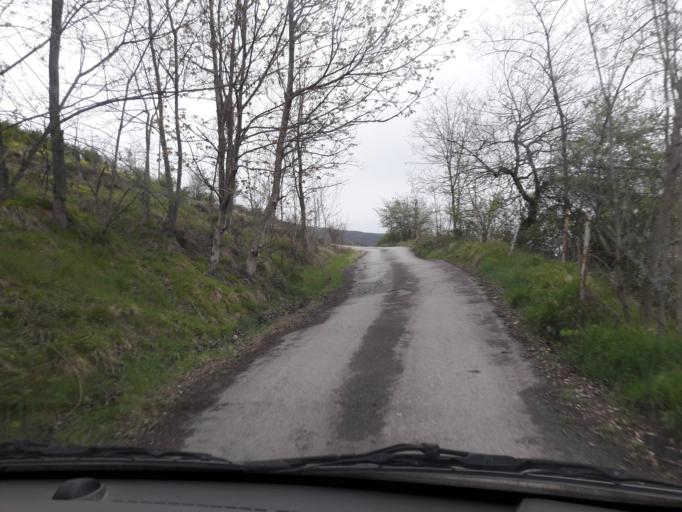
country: TR
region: Trabzon
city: Duzkoy
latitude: 40.9310
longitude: 39.4782
